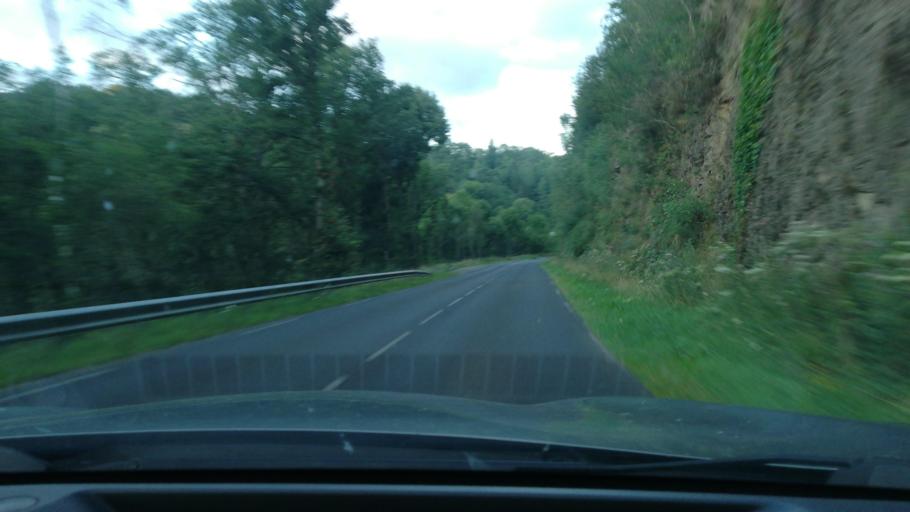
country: FR
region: Auvergne
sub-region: Departement du Cantal
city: Laroquebrou
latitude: 44.9676
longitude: 2.1815
